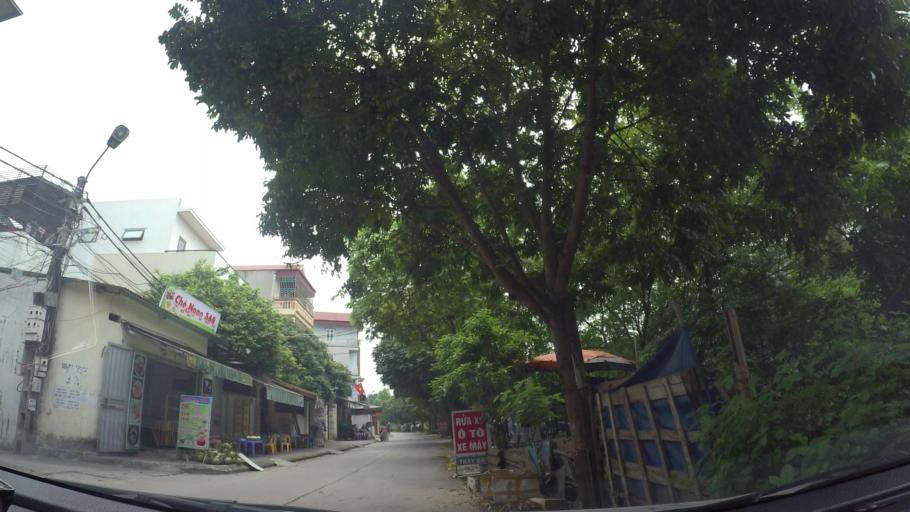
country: VN
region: Ha Noi
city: Ha Dong
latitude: 20.9709
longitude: 105.7583
